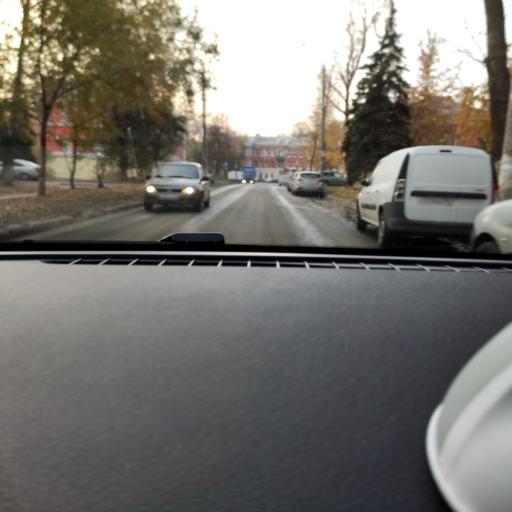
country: RU
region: Samara
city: Samara
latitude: 53.1991
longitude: 50.2192
